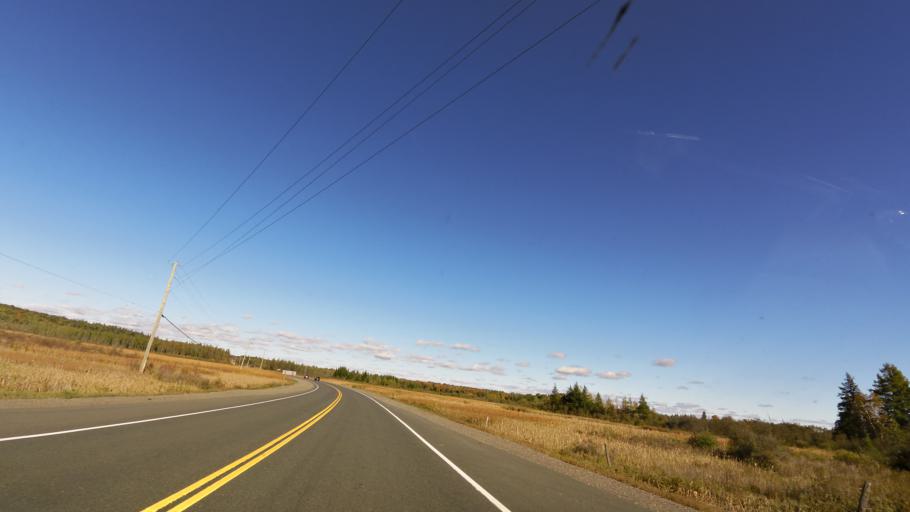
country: CA
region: Ontario
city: Thessalon
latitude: 46.2827
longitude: -83.4119
